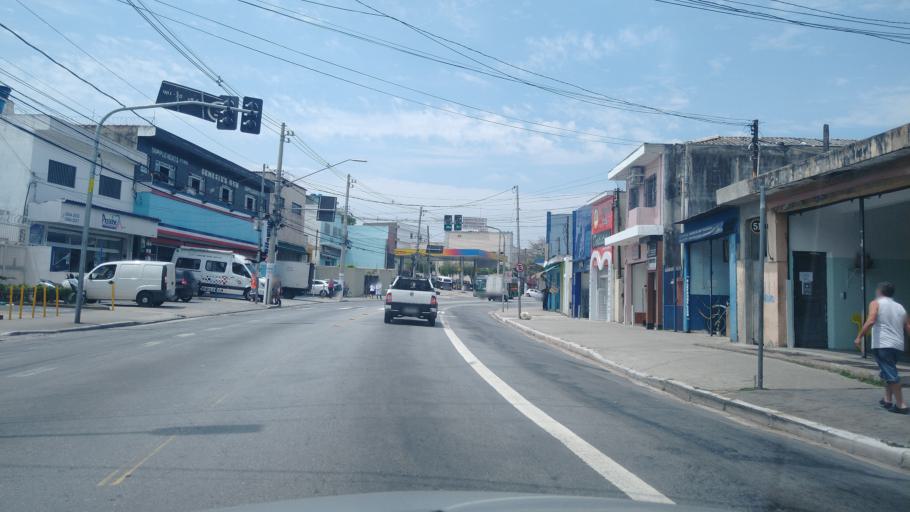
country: BR
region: Sao Paulo
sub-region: Sao Paulo
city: Sao Paulo
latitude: -23.4678
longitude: -46.6777
